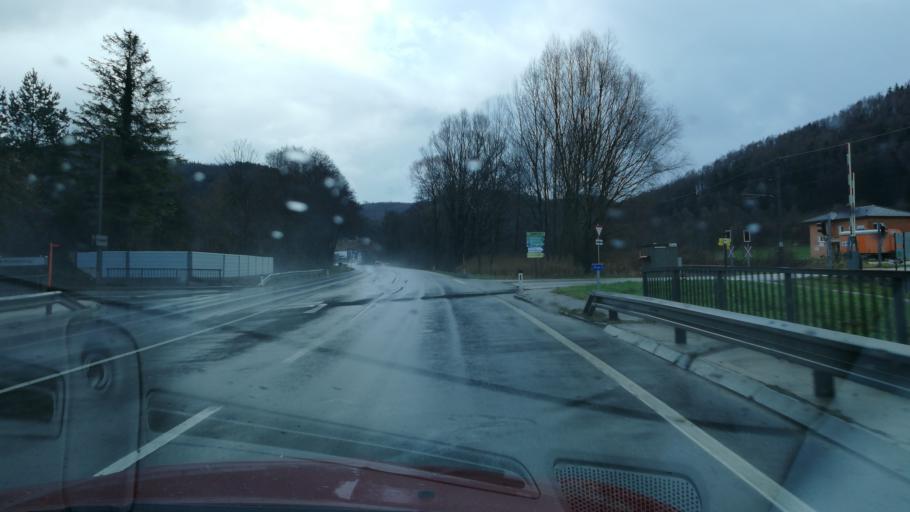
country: AT
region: Upper Austria
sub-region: Politischer Bezirk Kirchdorf an der Krems
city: Micheldorf in Oberoesterreich
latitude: 47.8700
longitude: 14.1368
